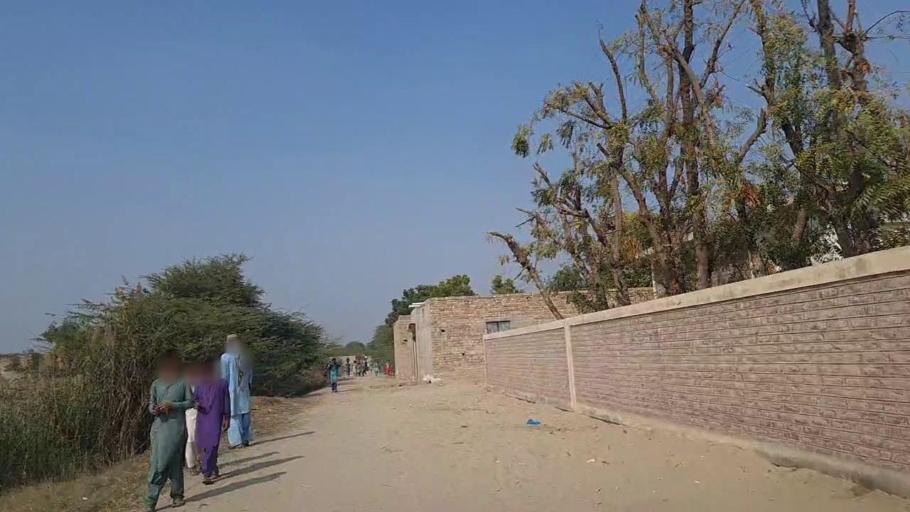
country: PK
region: Sindh
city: Daur
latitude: 26.4804
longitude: 68.4649
